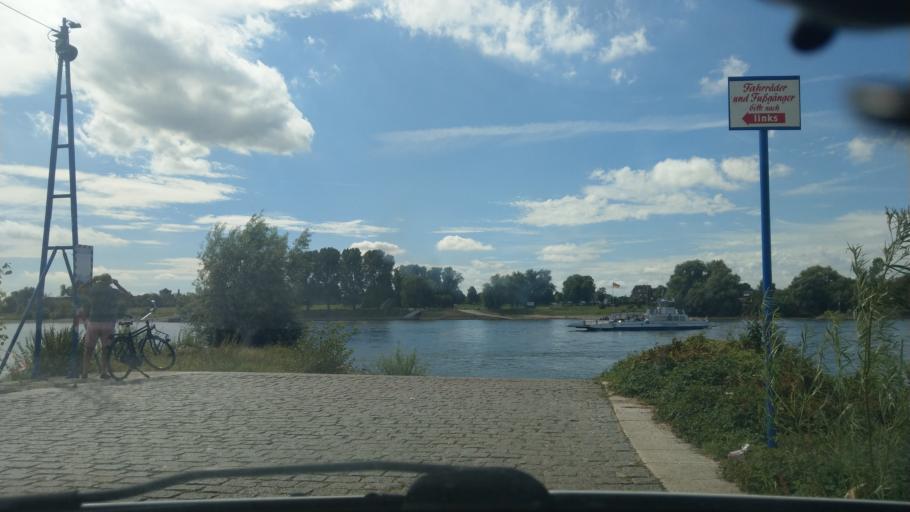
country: DE
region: North Rhine-Westphalia
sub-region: Regierungsbezirk Dusseldorf
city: Dormagen
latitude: 51.1301
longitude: 6.8545
